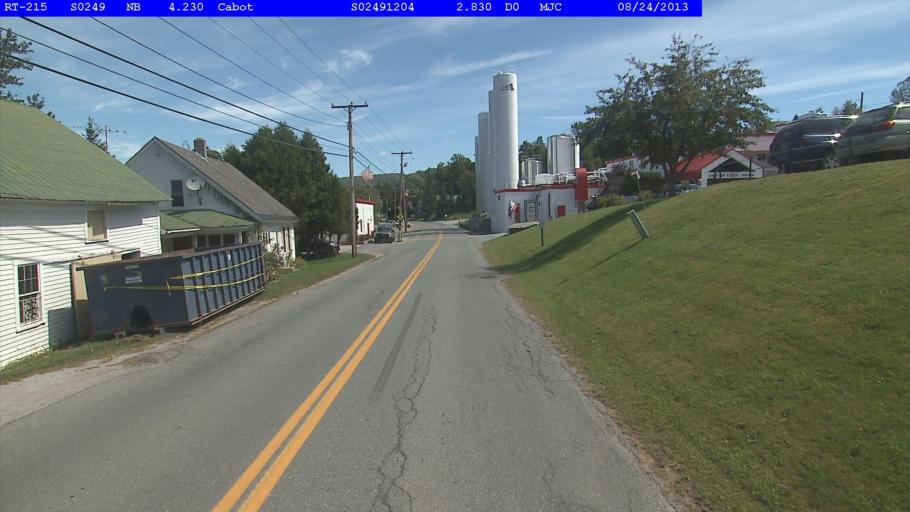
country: US
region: Vermont
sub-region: Caledonia County
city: Hardwick
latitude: 44.4003
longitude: -72.3155
